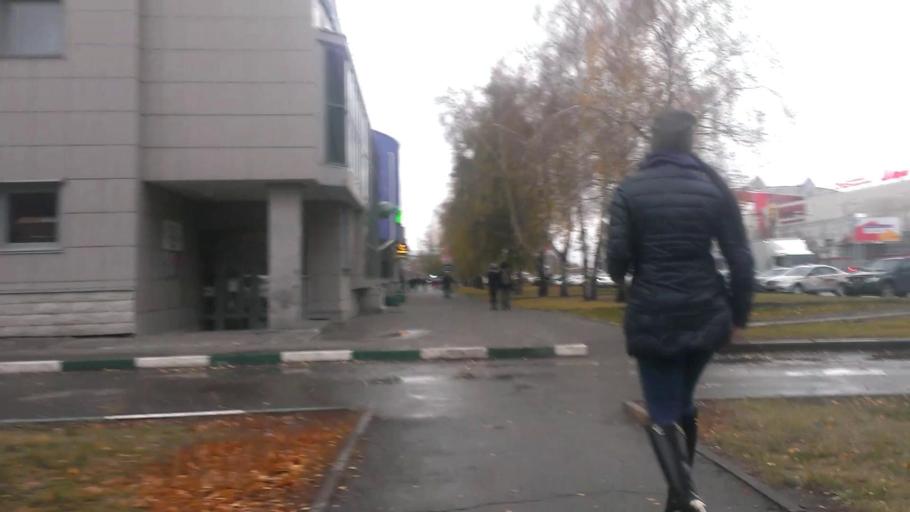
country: RU
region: Altai Krai
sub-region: Gorod Barnaulskiy
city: Barnaul
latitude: 53.3604
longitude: 83.6959
